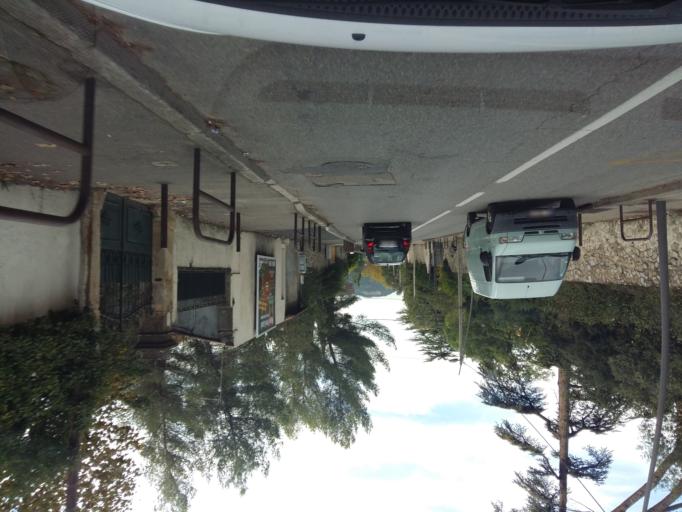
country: FR
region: Provence-Alpes-Cote d'Azur
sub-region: Departement des Bouches-du-Rhone
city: Aix-en-Provence
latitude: 43.5213
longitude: 5.4587
